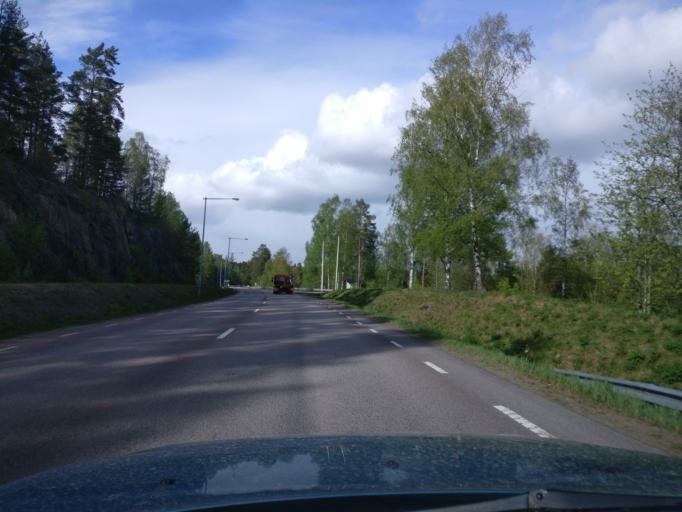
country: SE
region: Vaermland
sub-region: Forshaga Kommun
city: Forshaga
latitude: 59.5192
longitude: 13.4466
